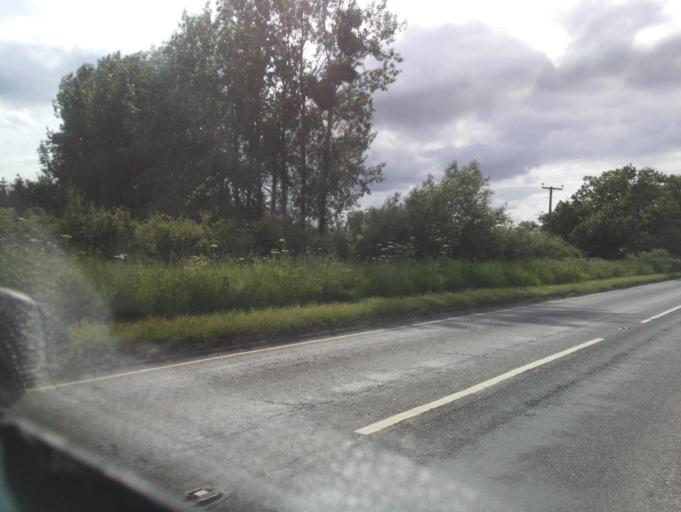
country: GB
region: England
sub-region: Worcestershire
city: Pershore
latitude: 52.1375
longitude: -2.1193
